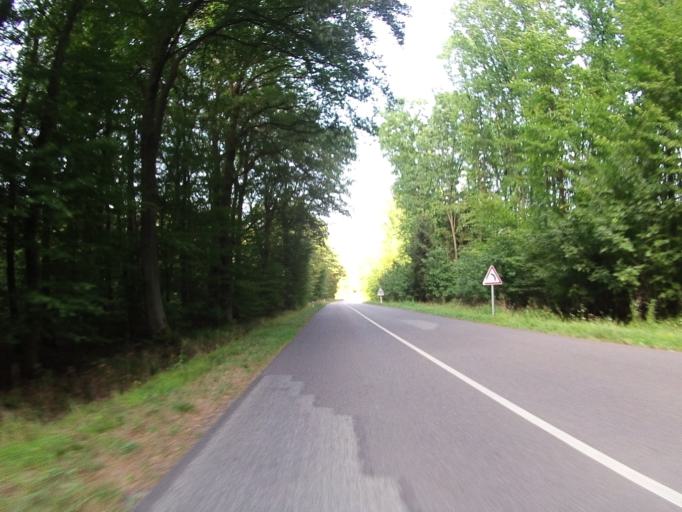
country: FR
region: Alsace
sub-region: Departement du Bas-Rhin
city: Seltz
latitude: 48.9069
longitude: 8.1144
